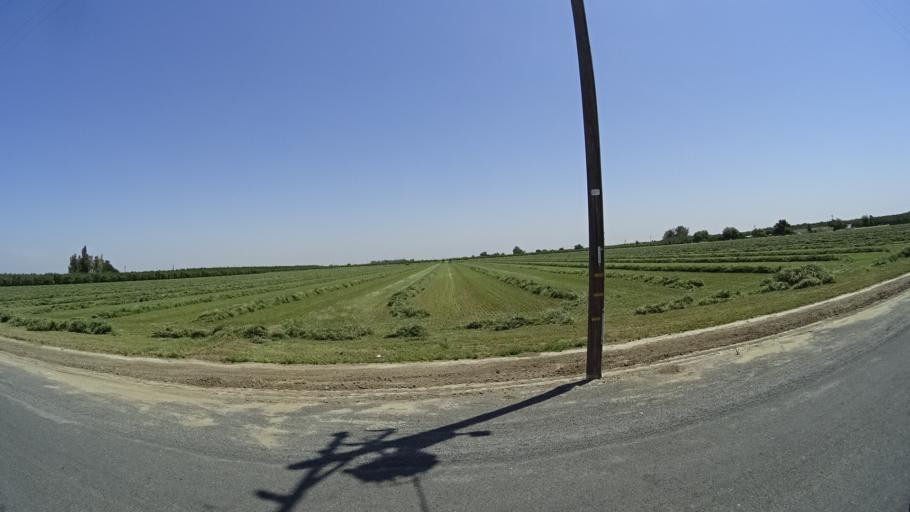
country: US
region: California
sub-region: Kings County
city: Armona
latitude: 36.2860
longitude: -119.7271
